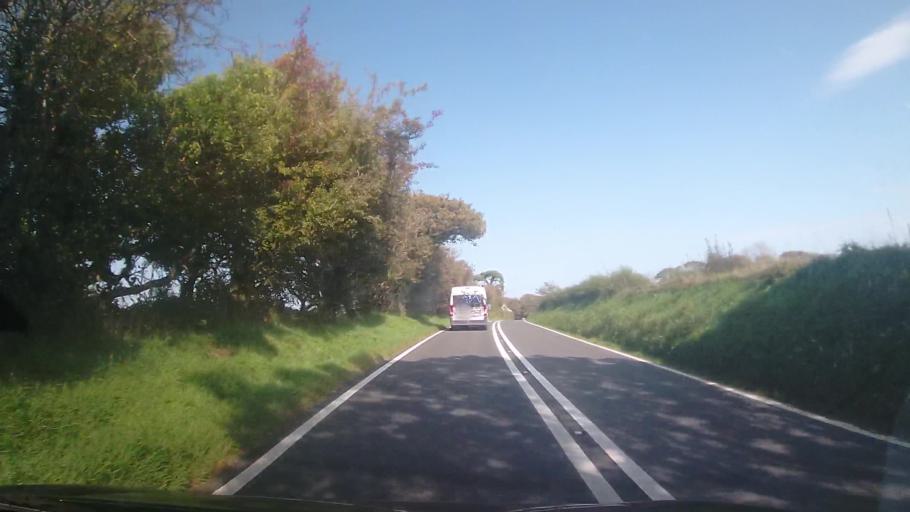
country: GB
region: Wales
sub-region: Pembrokeshire
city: Crymych
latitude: 52.0226
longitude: -4.6956
